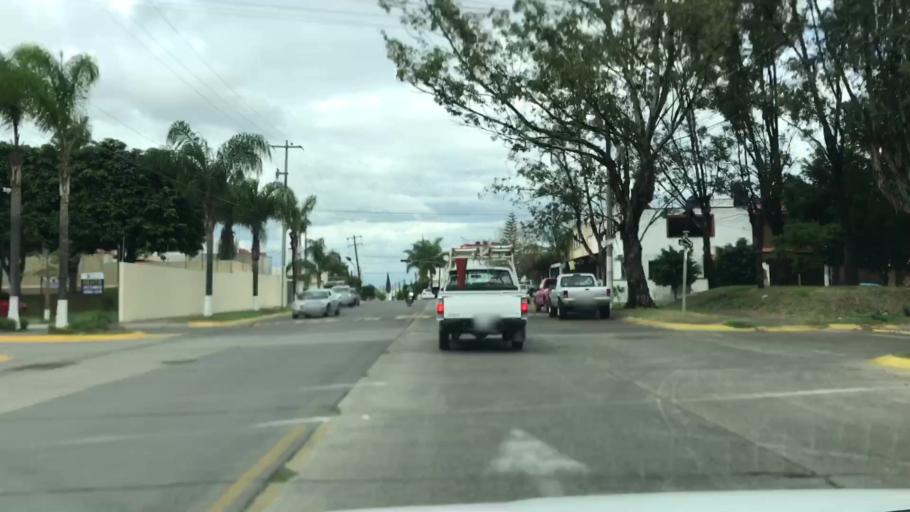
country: MX
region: Jalisco
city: Guadalajara
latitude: 20.6412
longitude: -103.4380
